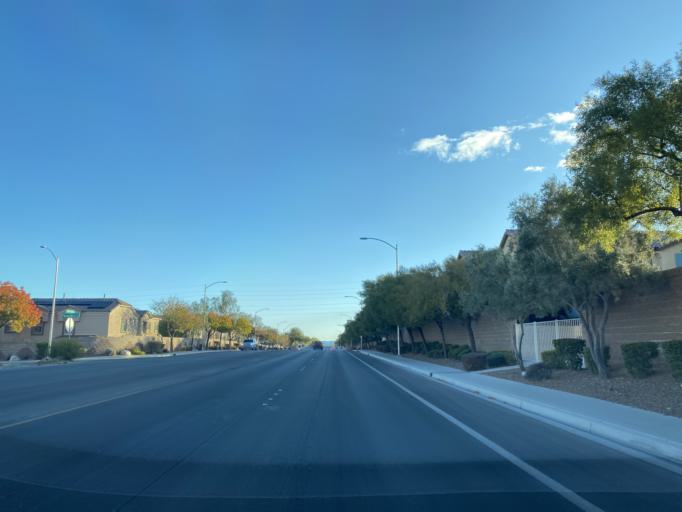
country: US
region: Nevada
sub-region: Clark County
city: Summerlin South
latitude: 36.3015
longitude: -115.3059
